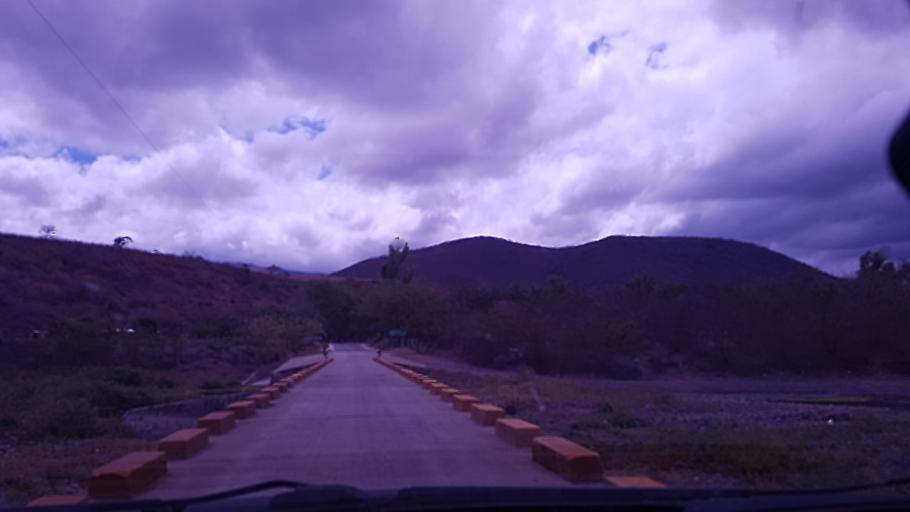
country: NI
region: Esteli
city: Condega
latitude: 13.3759
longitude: -86.3868
